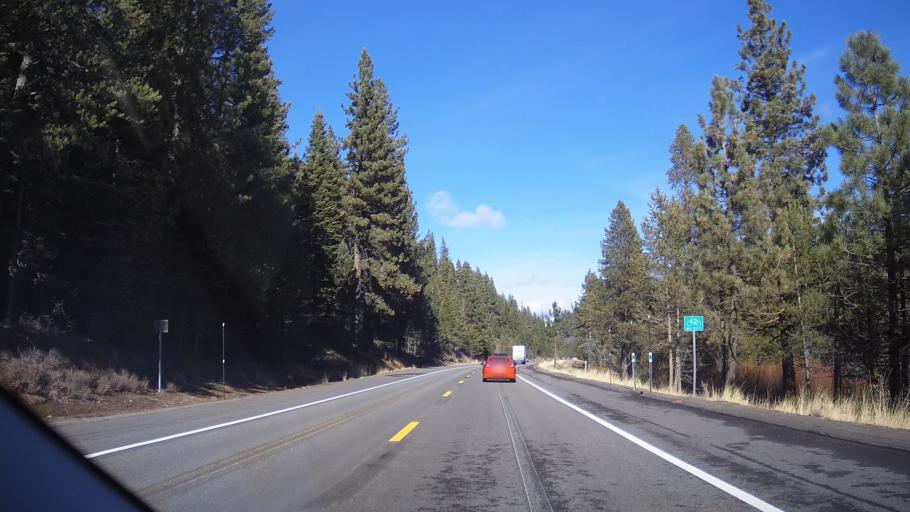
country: US
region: California
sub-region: Nevada County
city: Truckee
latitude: 39.2908
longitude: -120.2081
